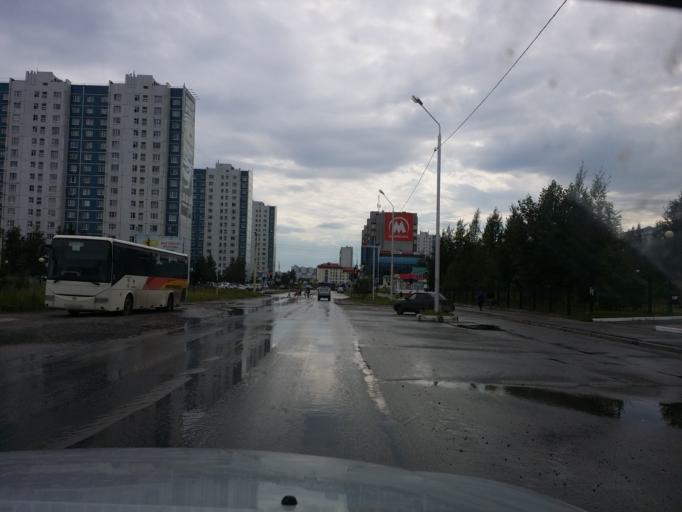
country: RU
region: Khanty-Mansiyskiy Avtonomnyy Okrug
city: Nizhnevartovsk
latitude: 60.9412
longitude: 76.5908
